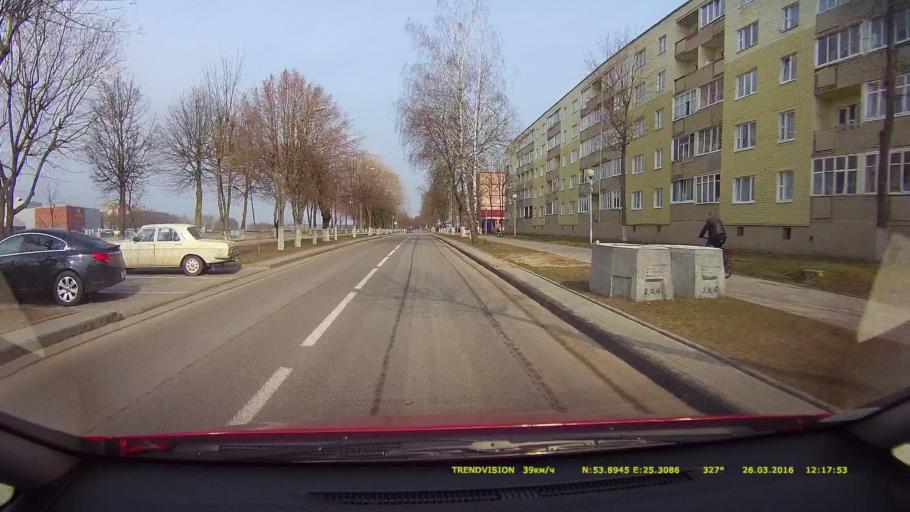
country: BY
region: Grodnenskaya
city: Lida
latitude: 53.8947
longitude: 25.3085
